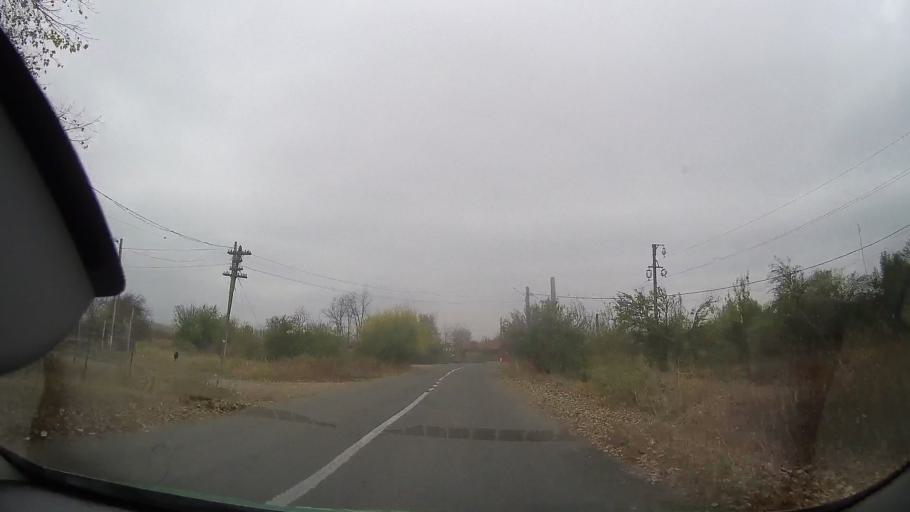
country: RO
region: Ialomita
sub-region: Comuna Grindu
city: Grindu
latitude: 44.7798
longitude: 26.9066
